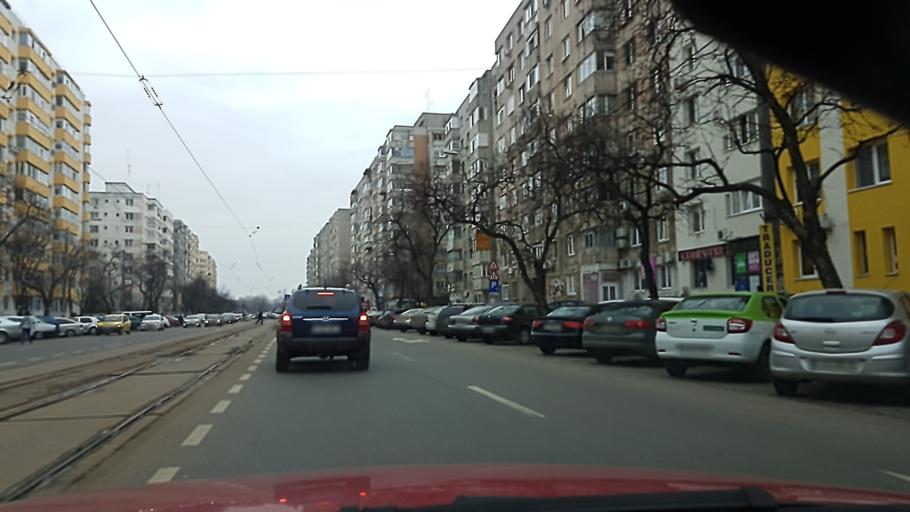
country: RO
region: Ilfov
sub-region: Comuna Fundeni-Dobroesti
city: Fundeni
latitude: 44.4394
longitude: 26.1580
